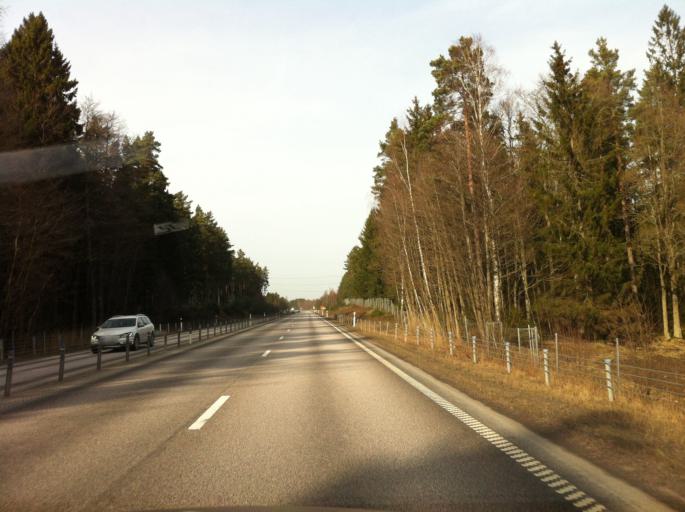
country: SE
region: Vaestra Goetaland
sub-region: Skovde Kommun
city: Stopen
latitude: 58.5042
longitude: 13.8402
